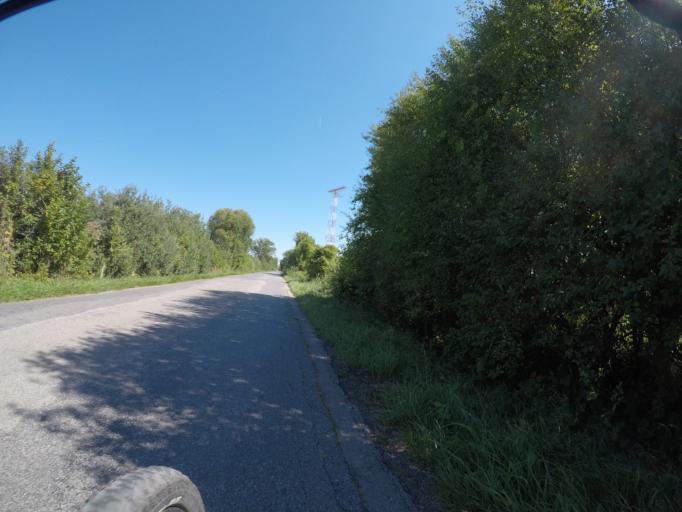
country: AT
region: Lower Austria
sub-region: Politischer Bezirk Wien-Umgebung
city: Moosbrunn
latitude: 48.0052
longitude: 16.4574
